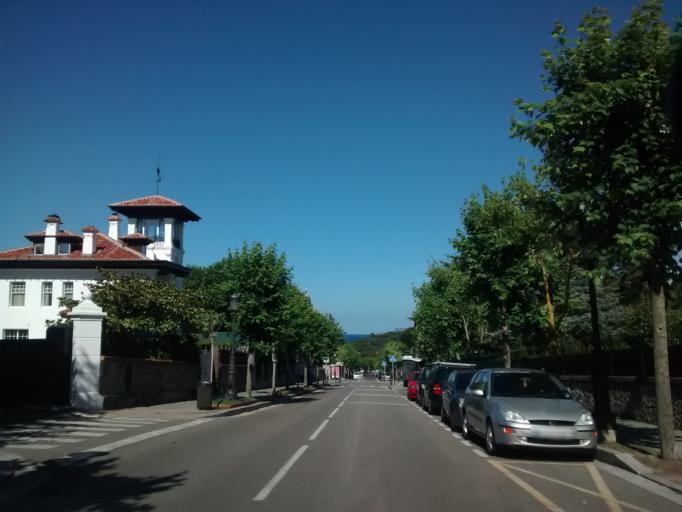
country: ES
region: Cantabria
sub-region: Provincia de Cantabria
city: Santander
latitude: 43.4671
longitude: -3.7808
